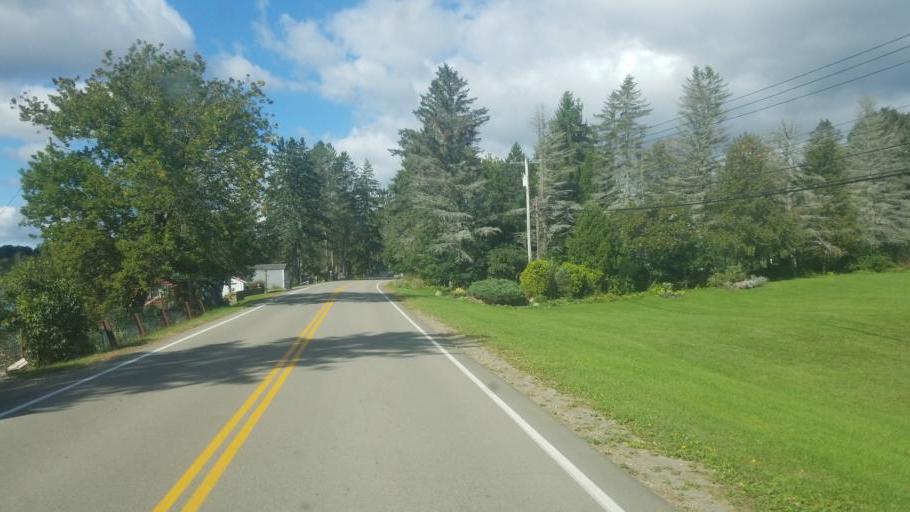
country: US
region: New York
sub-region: Allegany County
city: Cuba
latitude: 42.2594
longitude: -78.2946
